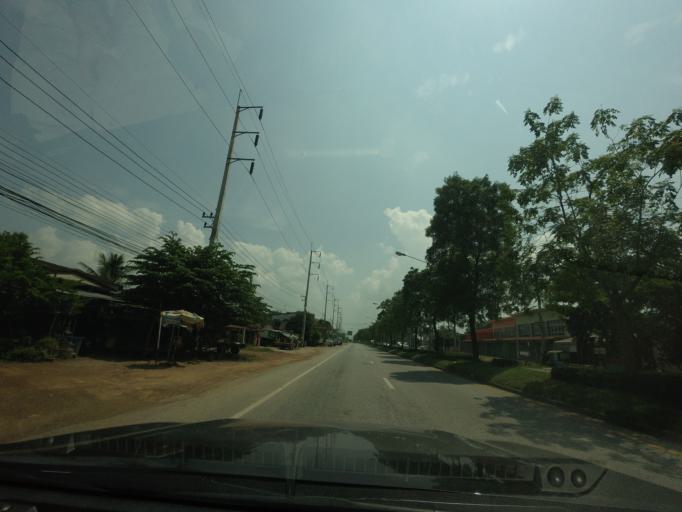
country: TH
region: Uttaradit
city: Uttaradit
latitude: 17.5898
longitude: 100.1344
